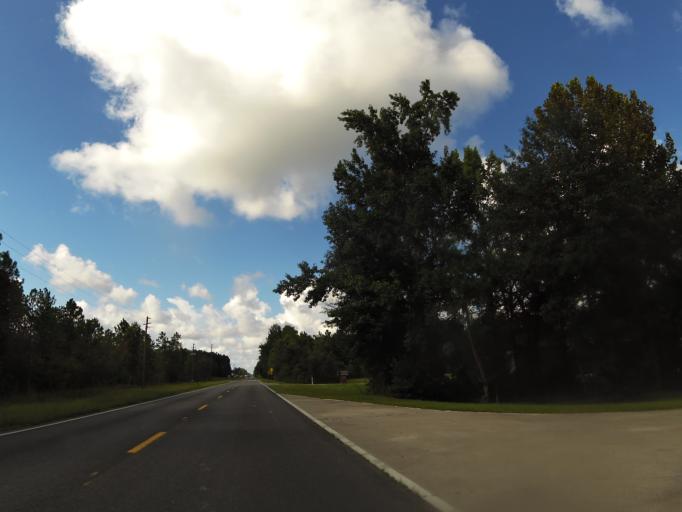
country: US
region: Georgia
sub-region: Camden County
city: Kingsland
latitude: 30.8160
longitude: -81.6933
